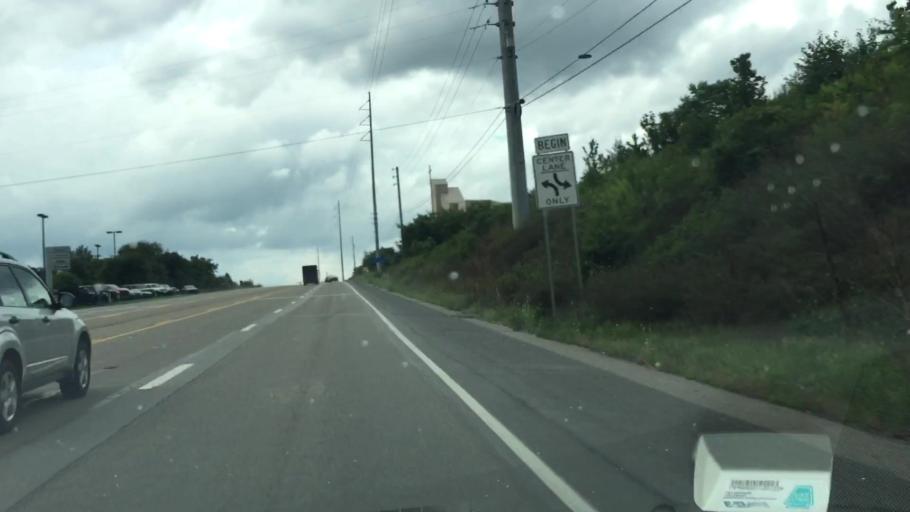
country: US
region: Pennsylvania
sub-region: Butler County
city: Fox Run
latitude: 40.7359
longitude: -80.1101
